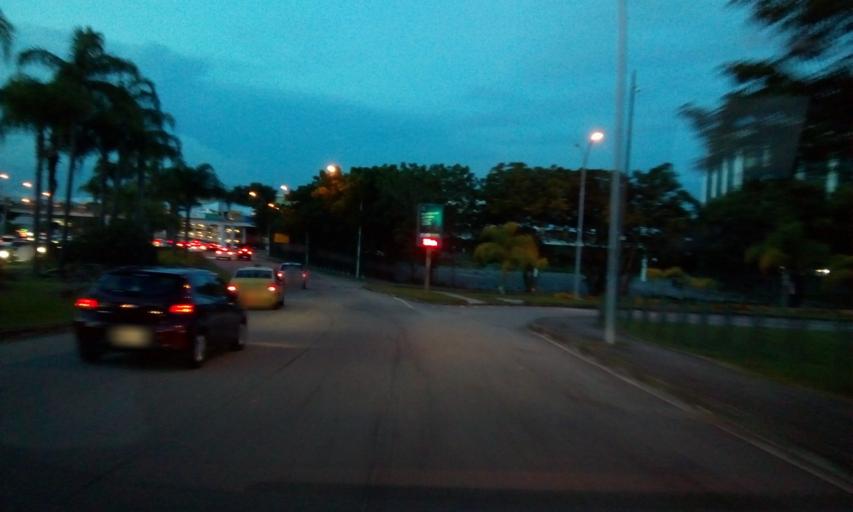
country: BR
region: Rio de Janeiro
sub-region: Rio De Janeiro
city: Rio de Janeiro
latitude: -22.9988
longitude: -43.3544
